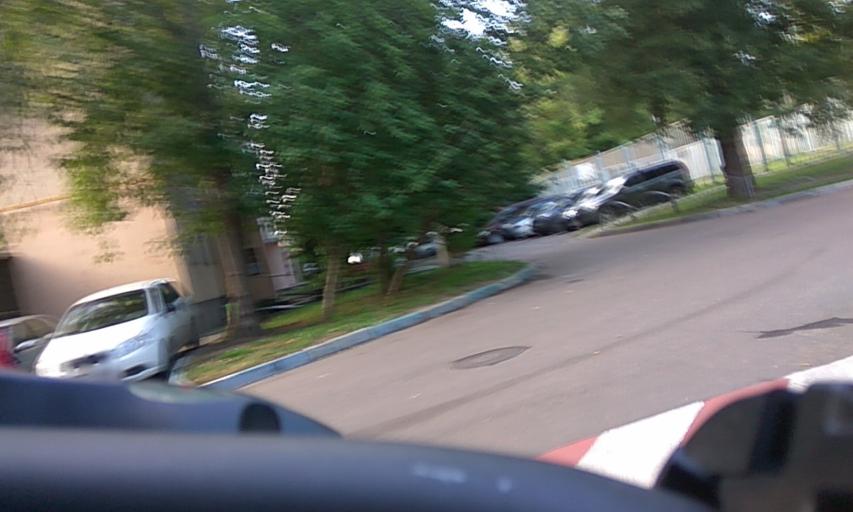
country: RU
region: Moscow
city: Kolomenskoye
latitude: 55.6796
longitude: 37.6850
